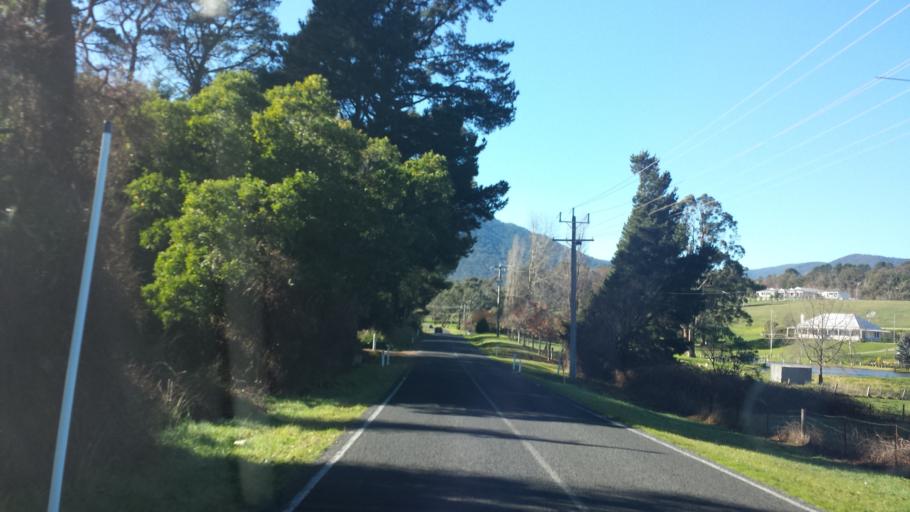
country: AU
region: Victoria
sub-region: Yarra Ranges
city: Healesville
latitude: -37.6711
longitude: 145.5175
